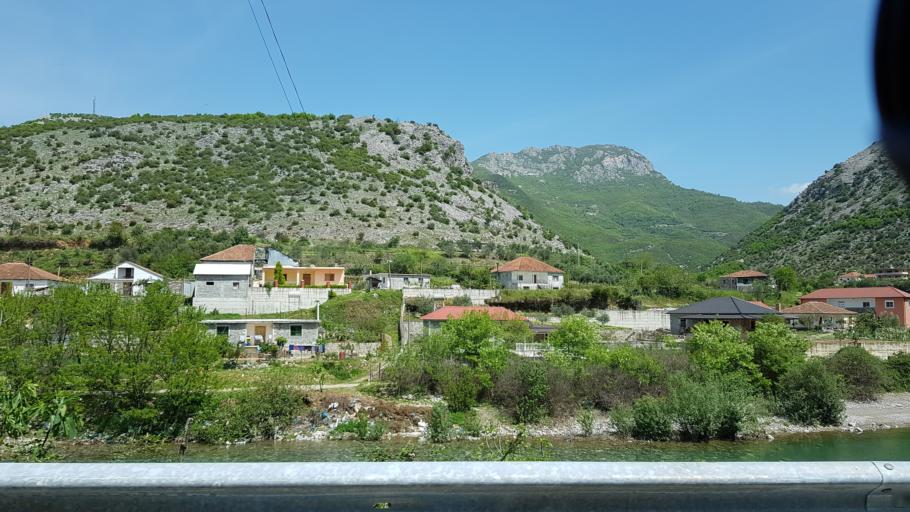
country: AL
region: Shkoder
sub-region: Rrethi i Shkodres
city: Guri i Zi
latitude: 42.1214
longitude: 19.6013
